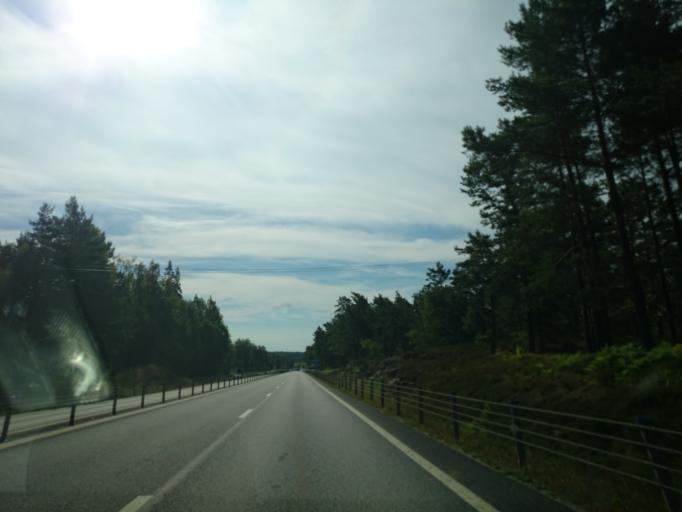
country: SE
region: Kalmar
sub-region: Vasterviks Kommun
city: Gamleby
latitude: 57.8140
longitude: 16.4853
